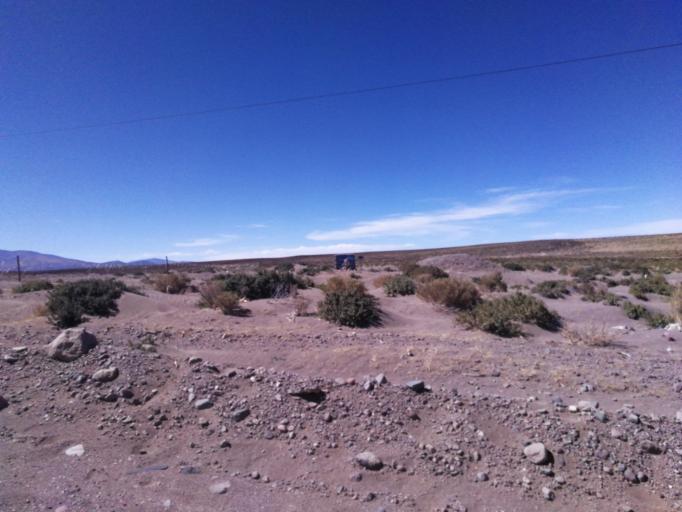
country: BO
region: Oruro
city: Cruz de Machacamarca
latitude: -19.2736
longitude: -68.2821
